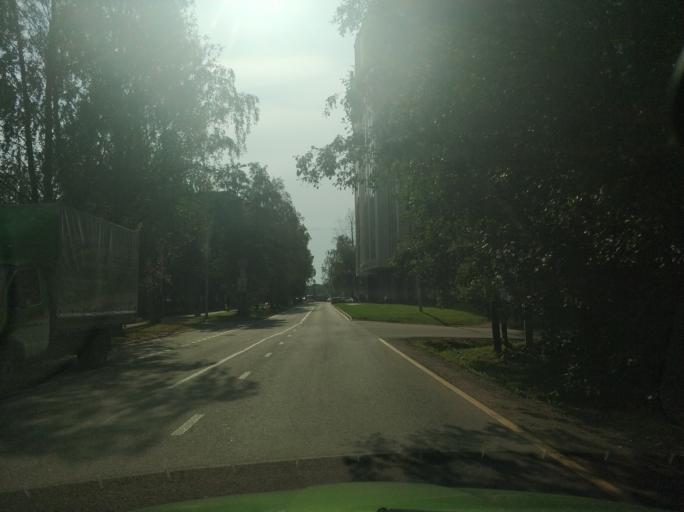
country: RU
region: Leningrad
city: Murino
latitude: 60.0436
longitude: 30.4637
